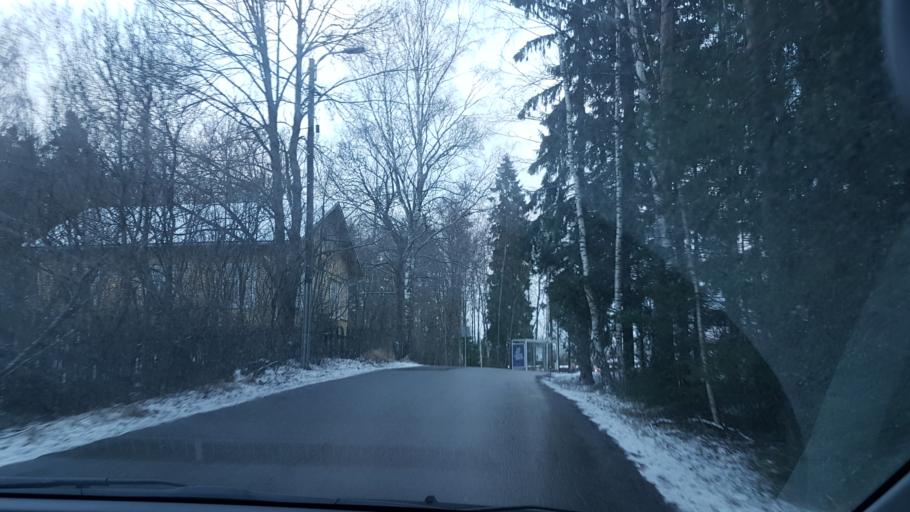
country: FI
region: Uusimaa
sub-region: Helsinki
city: Helsinki
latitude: 60.2797
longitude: 24.9223
